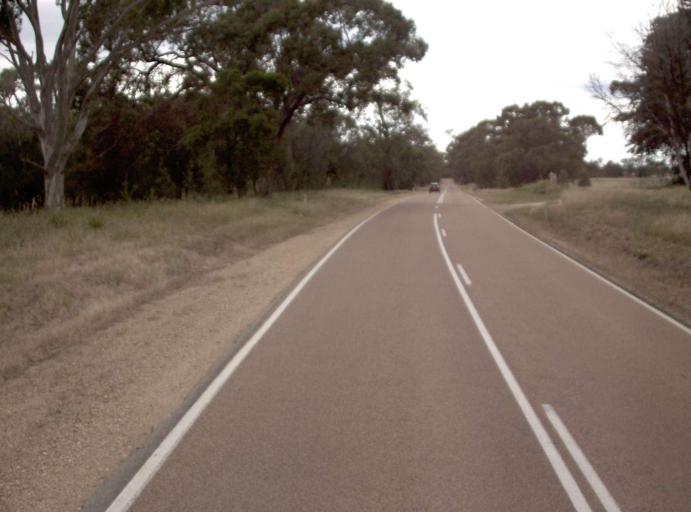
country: AU
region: Victoria
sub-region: Wellington
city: Sale
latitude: -38.0015
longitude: 147.3030
